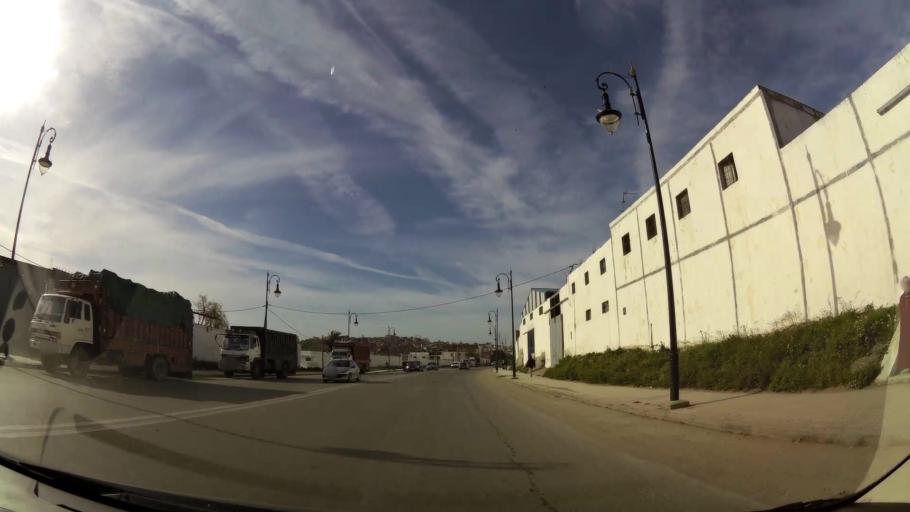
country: MA
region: Tanger-Tetouan
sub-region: Tanger-Assilah
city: Tangier
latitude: 35.7633
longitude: -5.7829
